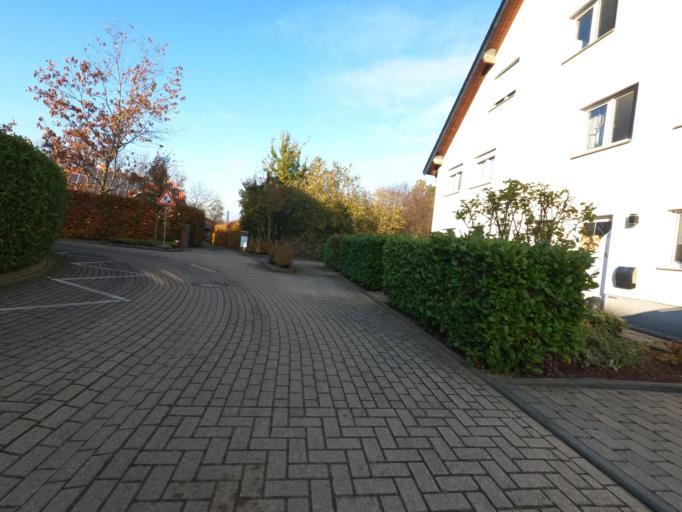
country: DE
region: North Rhine-Westphalia
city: Huckelhoven
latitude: 50.9973
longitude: 6.2124
